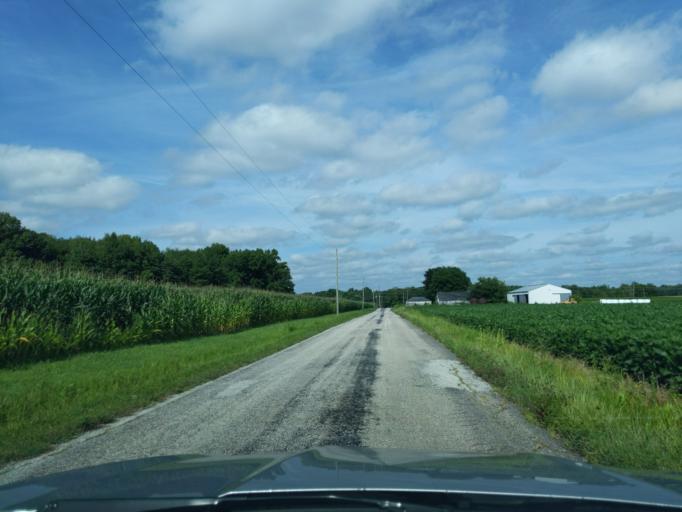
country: US
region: Indiana
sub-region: Ripley County
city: Osgood
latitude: 39.2402
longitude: -85.3518
